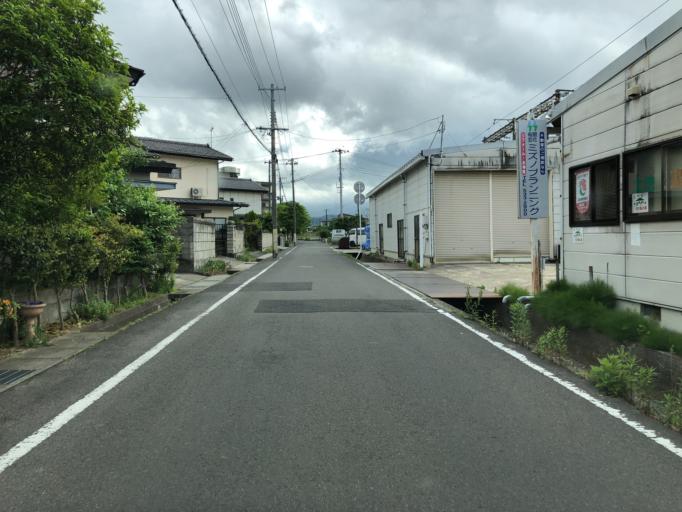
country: JP
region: Fukushima
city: Fukushima-shi
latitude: 37.7749
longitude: 140.4557
